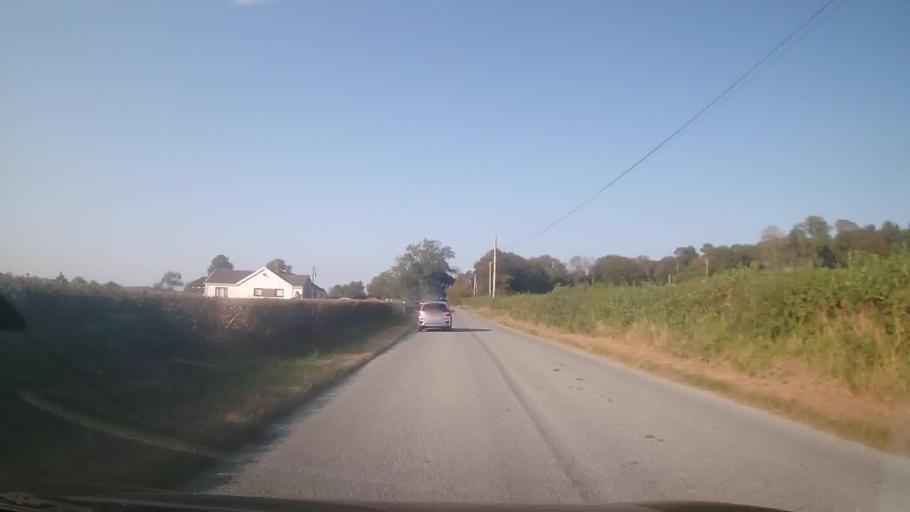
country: GB
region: Wales
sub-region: County of Ceredigion
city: Lledrod
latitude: 52.2267
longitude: -3.9315
